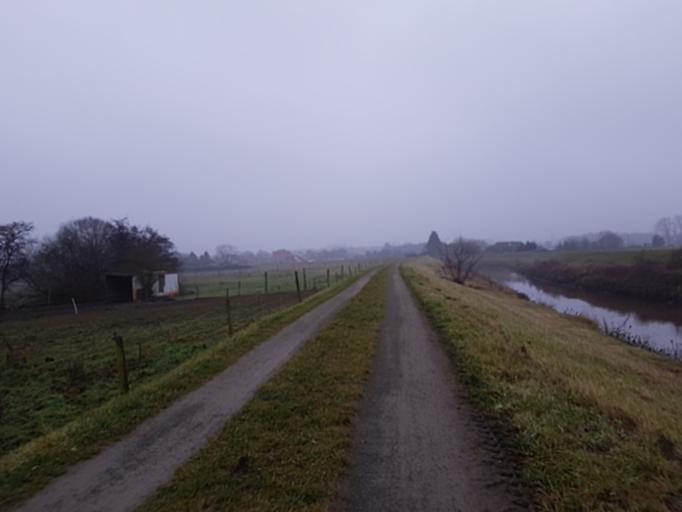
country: BE
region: Flanders
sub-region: Provincie Vlaams-Brabant
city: Haacht
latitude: 50.9895
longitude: 4.6402
